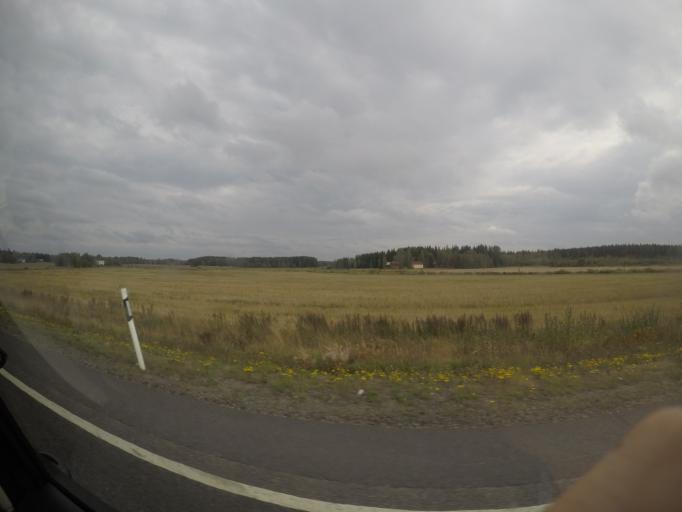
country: FI
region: Haeme
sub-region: Haemeenlinna
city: Parola
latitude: 61.0946
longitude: 24.4041
